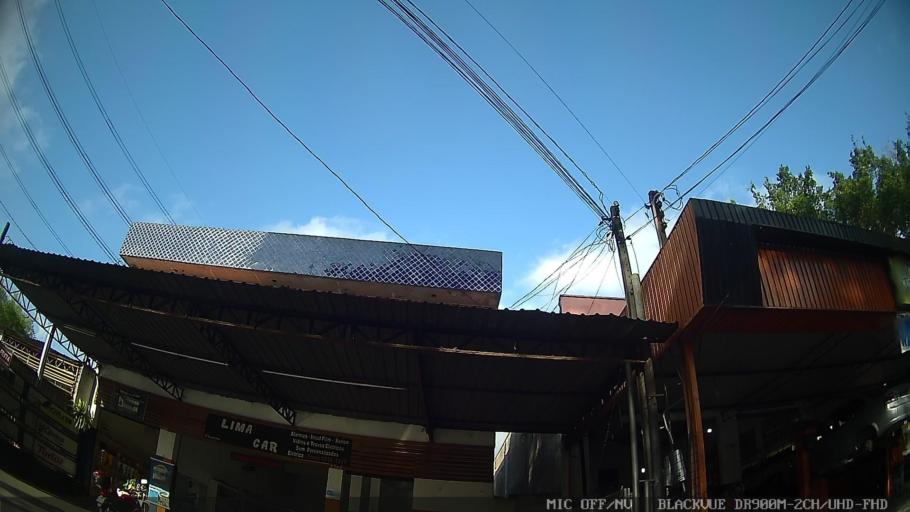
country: BR
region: Sao Paulo
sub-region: Taboao Da Serra
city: Taboao da Serra
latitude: -23.6420
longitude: -46.7661
